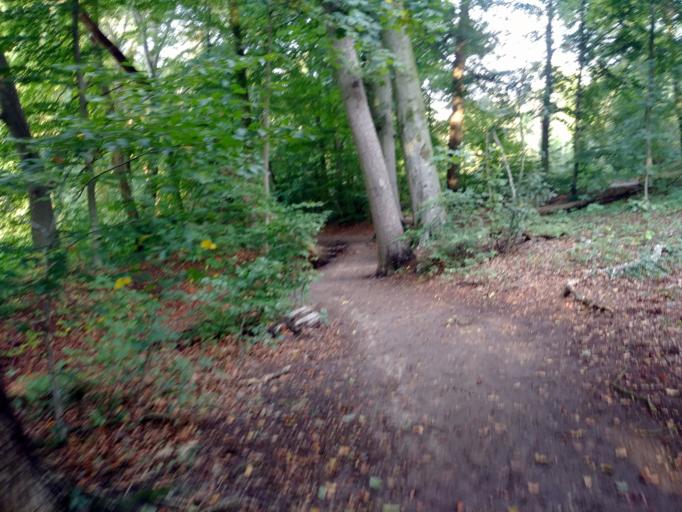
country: NL
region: Gelderland
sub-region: Gemeente Renkum
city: Renkum
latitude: 51.9885
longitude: 5.7309
